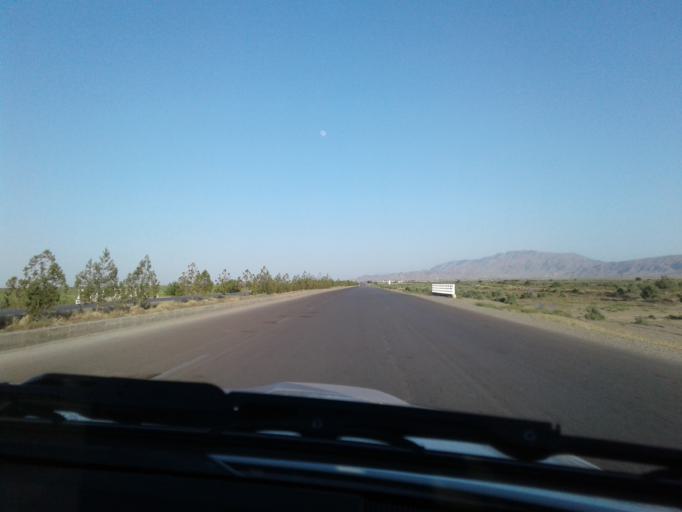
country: TM
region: Ahal
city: Baharly
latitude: 38.3565
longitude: 57.5389
